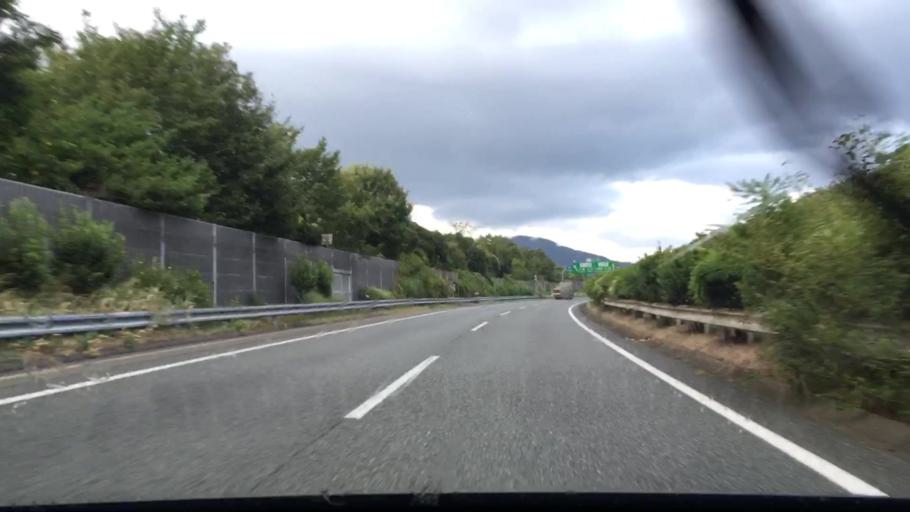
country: JP
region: Fukuoka
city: Kitakyushu
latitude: 33.8102
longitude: 130.8794
